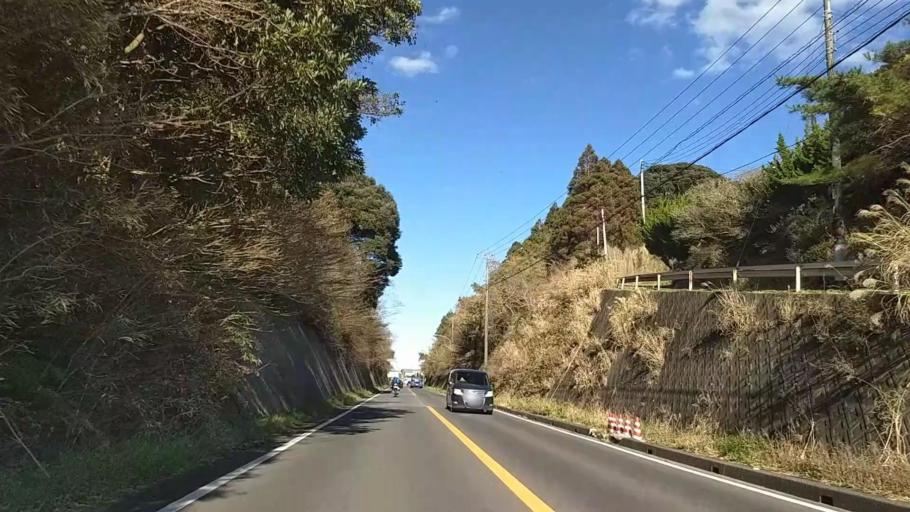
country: JP
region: Chiba
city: Ohara
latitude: 35.2153
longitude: 140.3773
